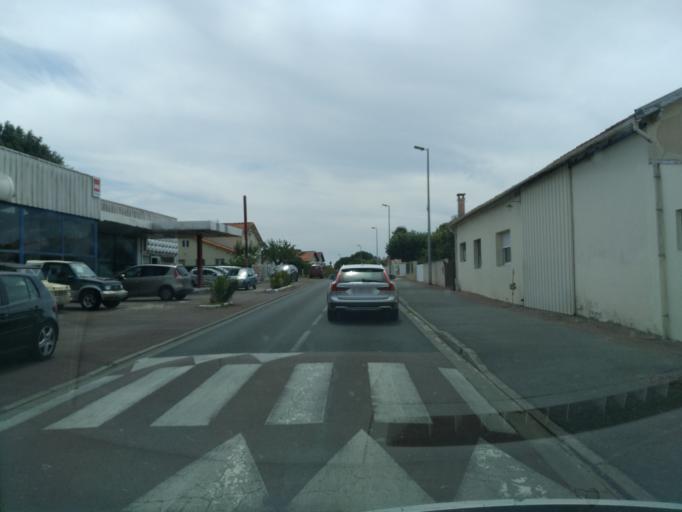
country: FR
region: Poitou-Charentes
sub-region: Departement de la Charente-Maritime
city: Saint-Palais-sur-Mer
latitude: 45.6467
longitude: -1.0838
